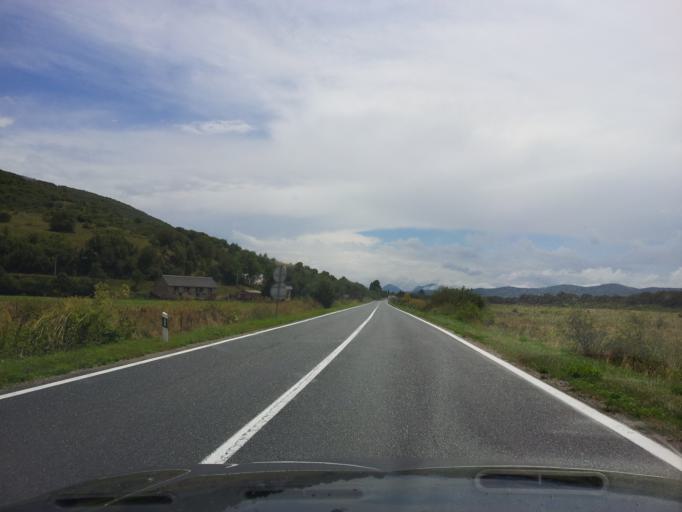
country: BA
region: Federation of Bosnia and Herzegovina
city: Bihac
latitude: 44.6069
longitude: 15.7364
